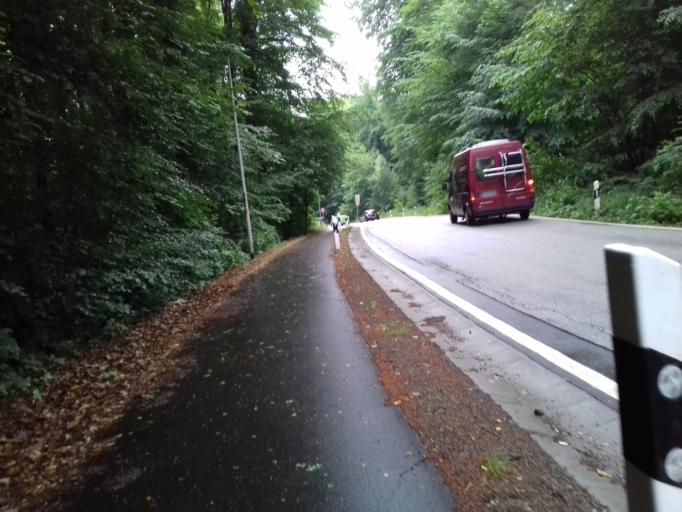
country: DE
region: Schleswig-Holstein
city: Kronshagen
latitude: 54.3213
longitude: 10.0741
